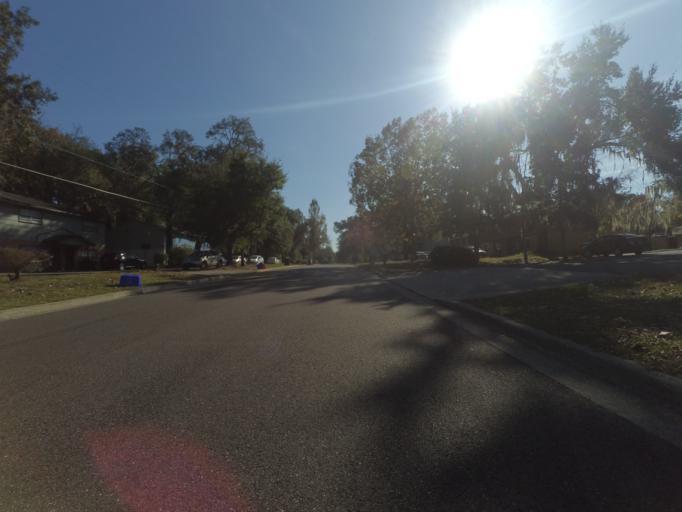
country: US
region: Florida
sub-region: Alachua County
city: Gainesville
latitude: 29.6188
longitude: -82.3656
